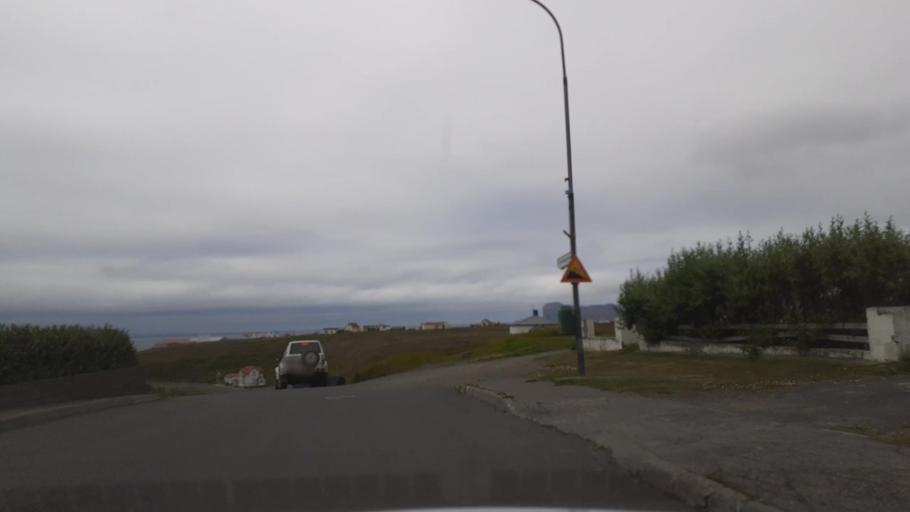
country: IS
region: Northwest
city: Saudarkrokur
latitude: 65.8976
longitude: -19.4142
